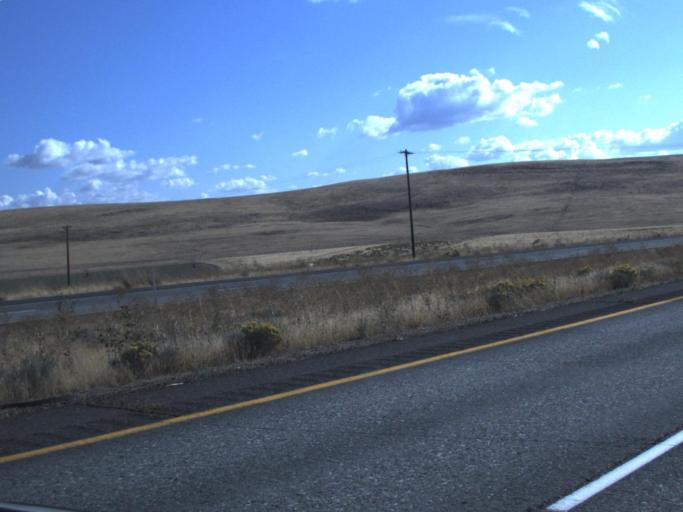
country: US
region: Oregon
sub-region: Umatilla County
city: Umatilla
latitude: 46.0181
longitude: -119.2268
